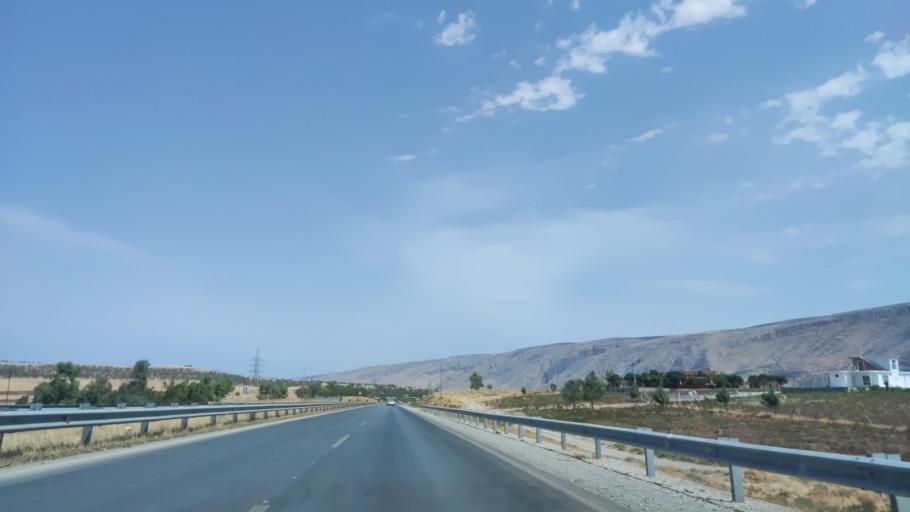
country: IQ
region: Arbil
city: Shaqlawah
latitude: 36.4737
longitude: 44.3813
